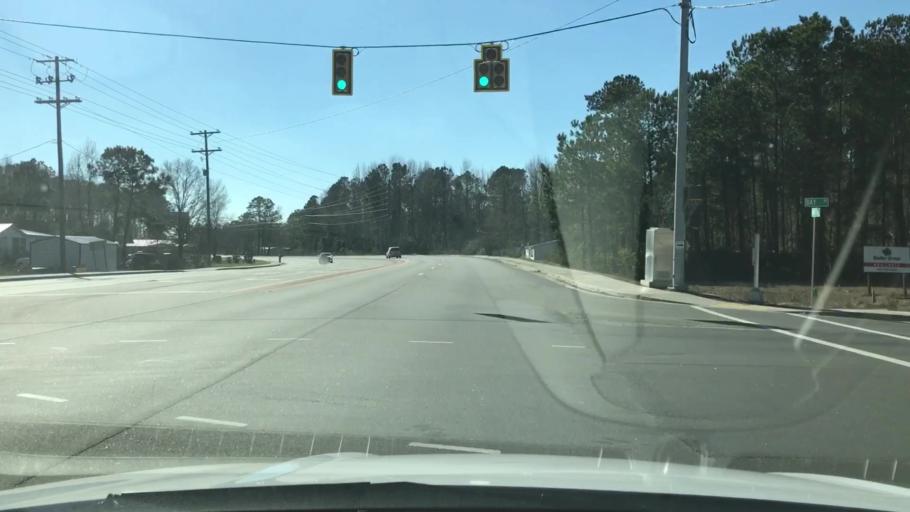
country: US
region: South Carolina
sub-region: Horry County
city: Garden City
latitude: 33.6390
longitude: -79.0320
